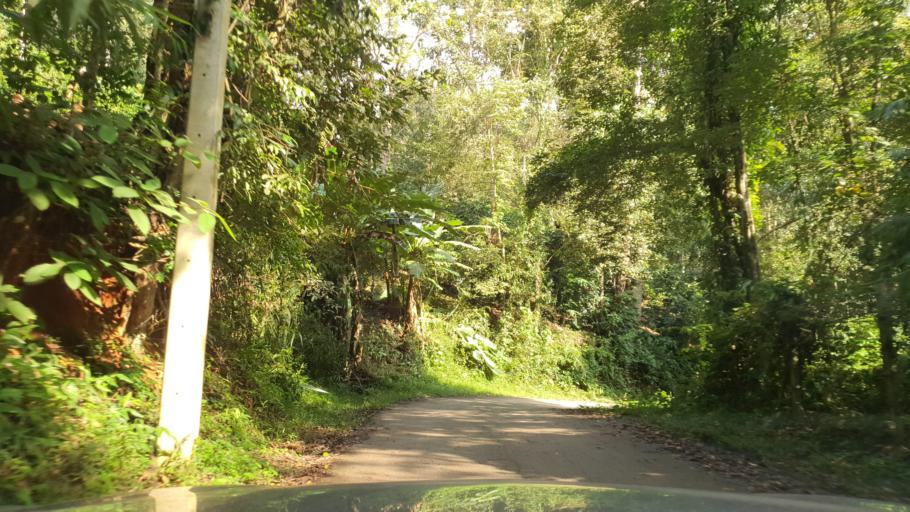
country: TH
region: Chiang Mai
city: Mae On
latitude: 18.9284
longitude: 99.3113
